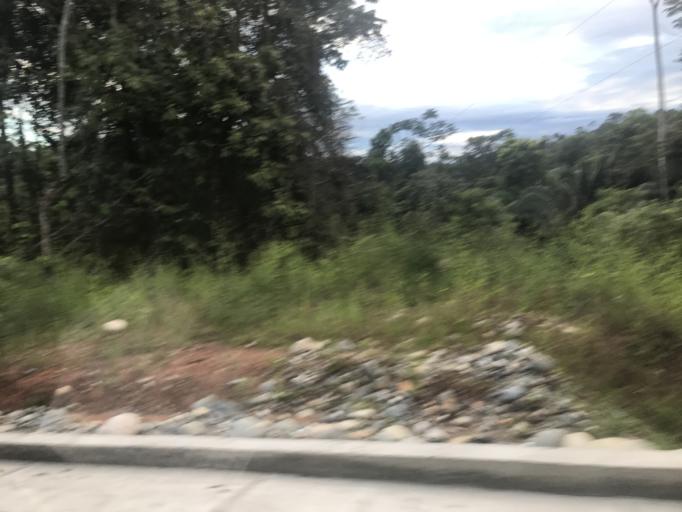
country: EC
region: Napo
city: Tena
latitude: -1.0587
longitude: -77.7000
